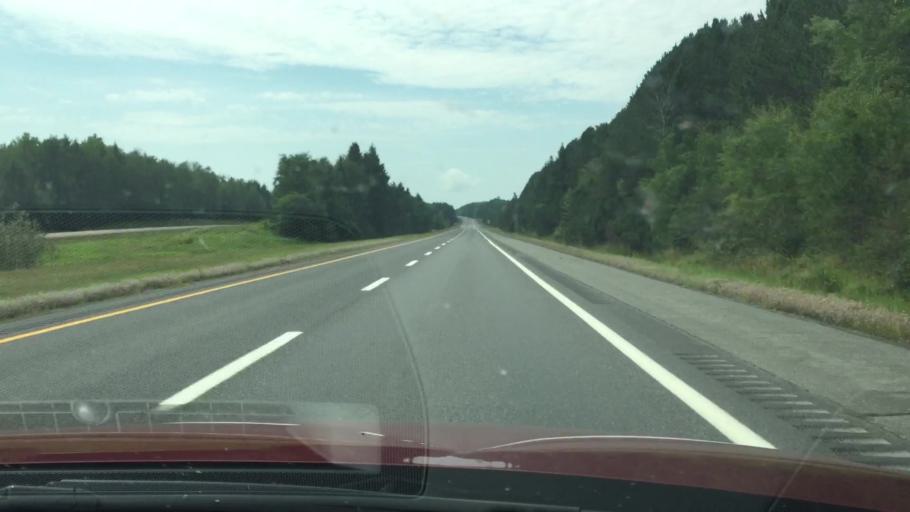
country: US
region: Maine
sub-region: Aroostook County
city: Hodgdon
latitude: 46.1409
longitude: -68.0707
